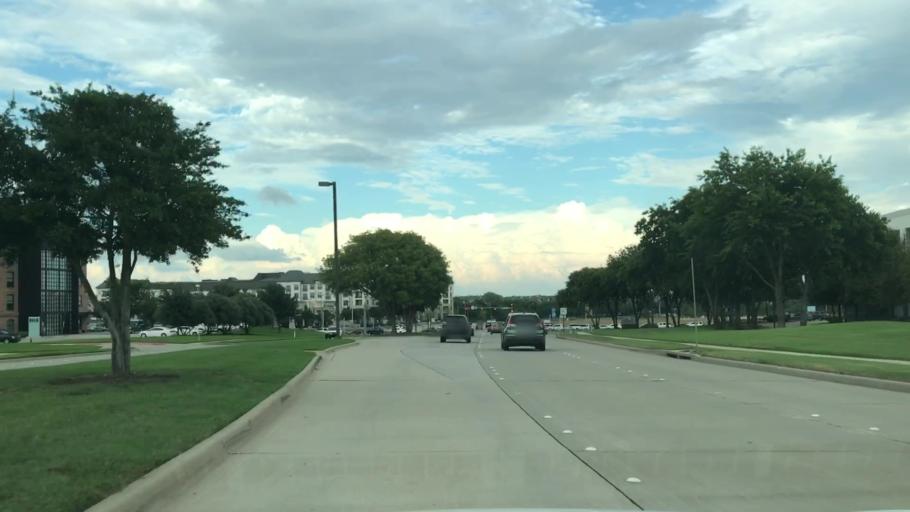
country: US
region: Texas
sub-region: Collin County
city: Frisco
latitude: 33.0877
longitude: -96.8074
